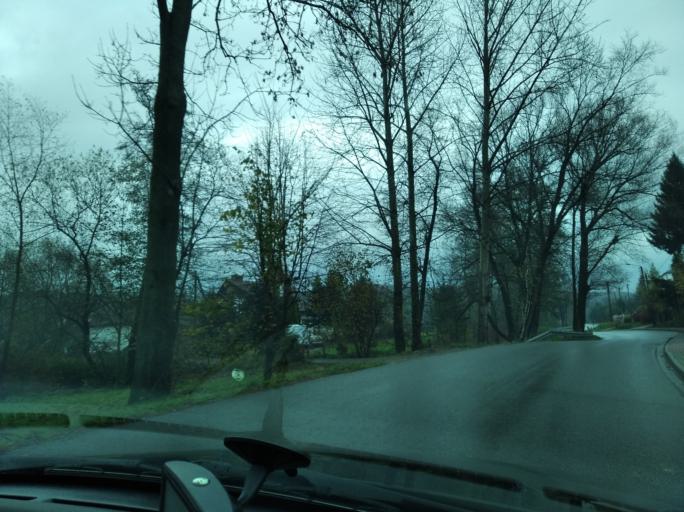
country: PL
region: Subcarpathian Voivodeship
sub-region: Powiat rzeszowski
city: Lubenia
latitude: 49.9209
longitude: 21.9538
